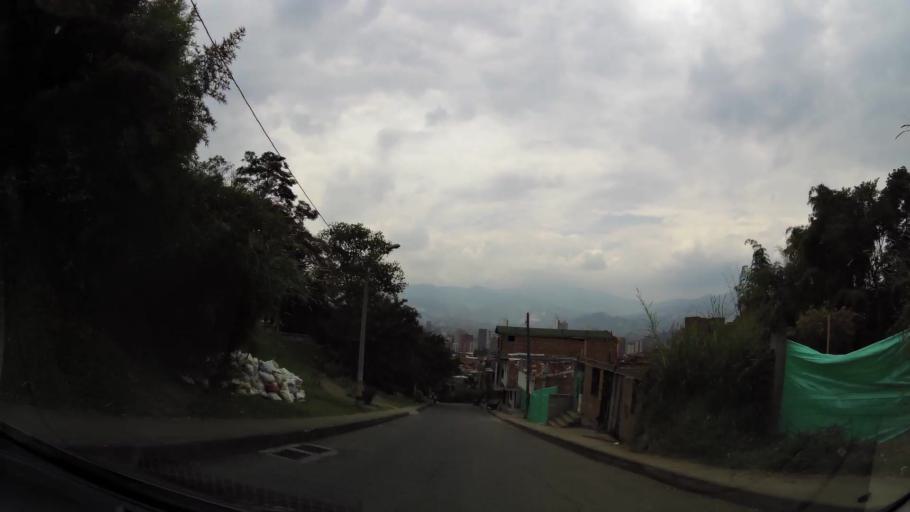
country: CO
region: Antioquia
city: Medellin
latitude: 6.2464
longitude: -75.5505
